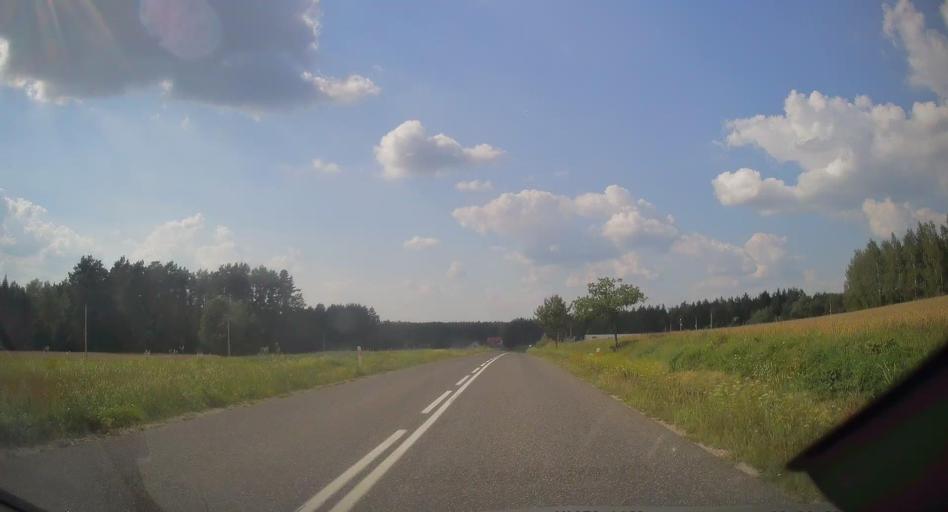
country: PL
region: Swietokrzyskie
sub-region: Powiat kielecki
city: Lopuszno
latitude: 50.8938
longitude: 20.2539
